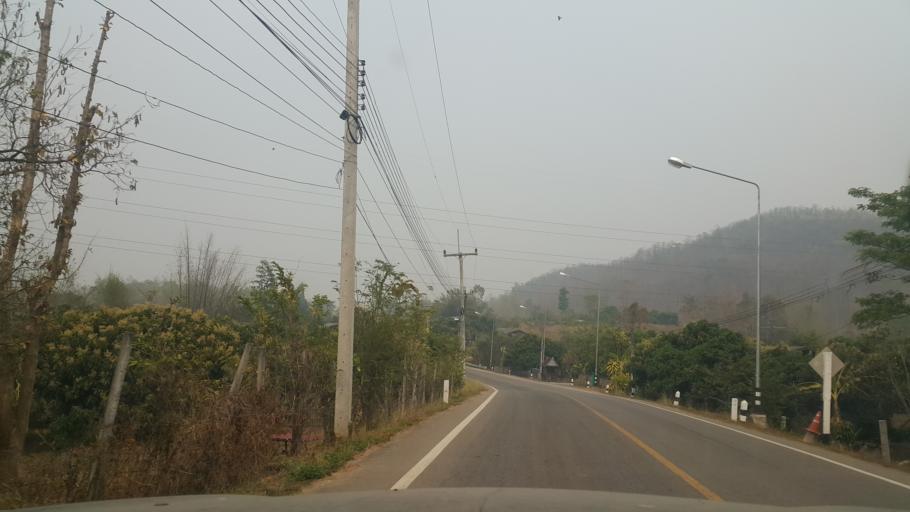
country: TH
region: Lamphun
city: Mae Tha
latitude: 18.4691
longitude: 99.1806
